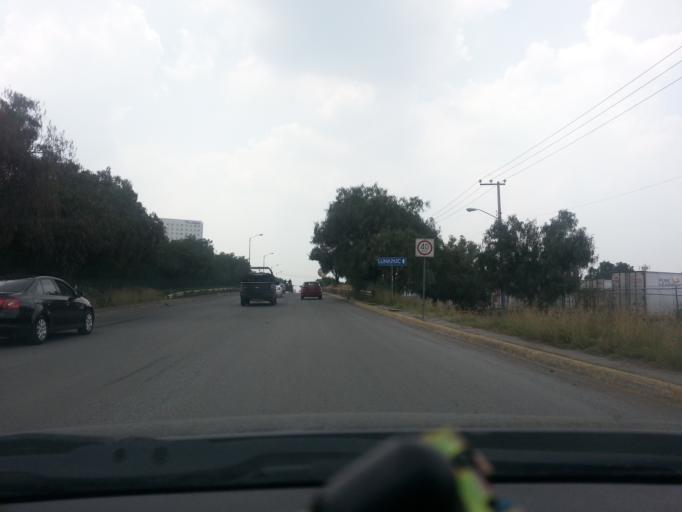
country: MX
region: Mexico
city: Cuautitlan Izcalli
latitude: 19.6583
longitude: -99.2053
